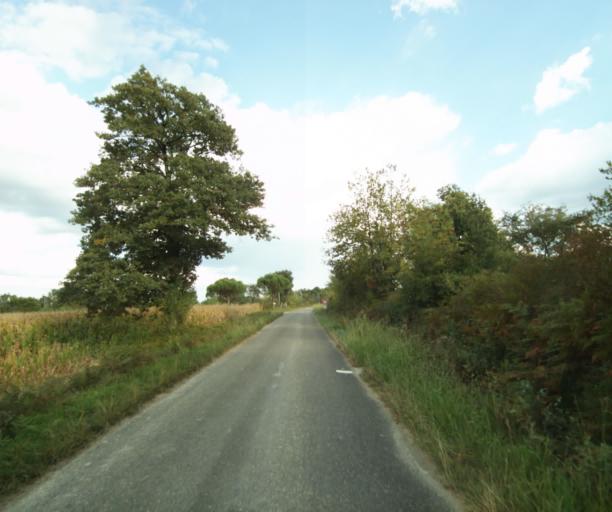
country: FR
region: Midi-Pyrenees
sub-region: Departement du Gers
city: Cazaubon
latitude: 43.9053
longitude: -0.0868
